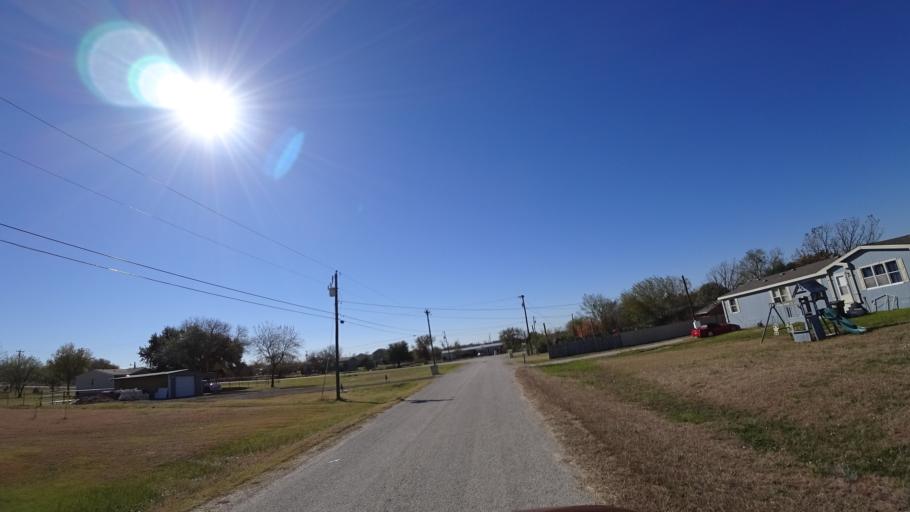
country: US
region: Texas
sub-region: Travis County
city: Garfield
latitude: 30.1106
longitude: -97.5983
